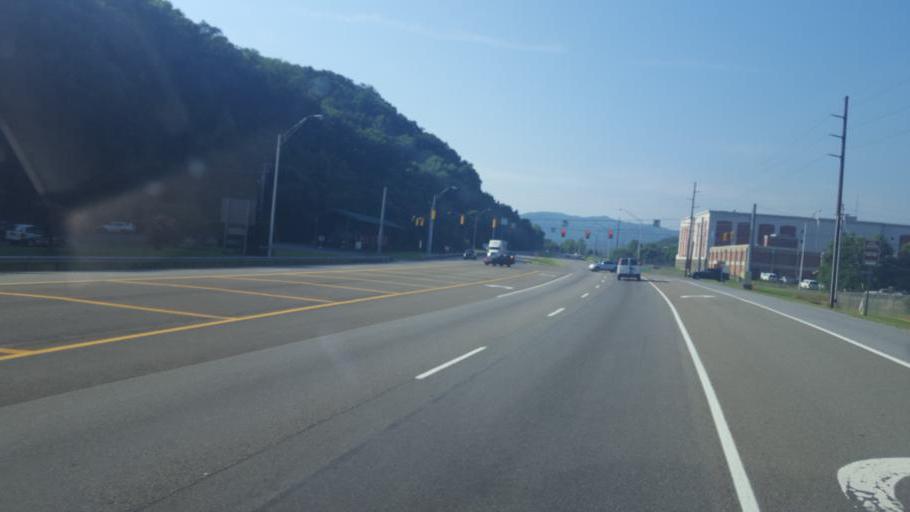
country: US
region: Tennessee
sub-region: Carter County
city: Elizabethton
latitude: 36.3499
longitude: -82.2084
